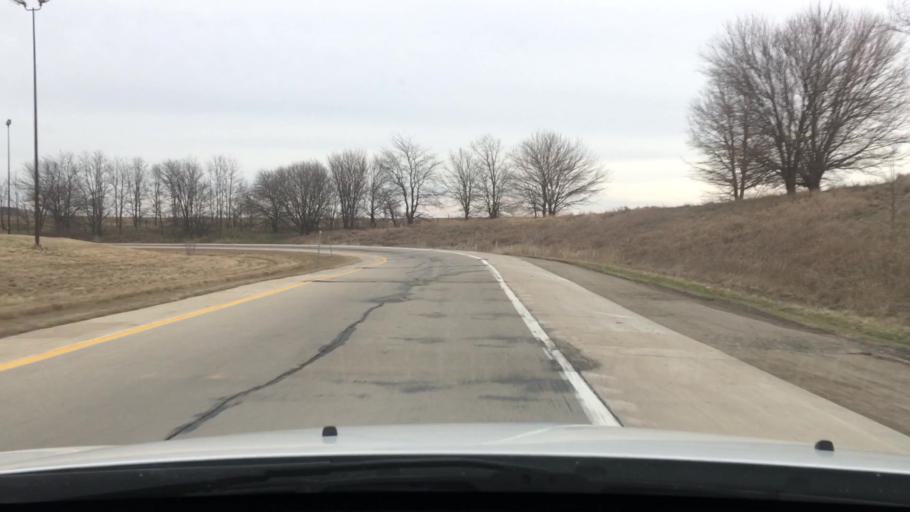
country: US
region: Illinois
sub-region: McLean County
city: Twin Grove
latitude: 40.3604
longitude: -89.1052
